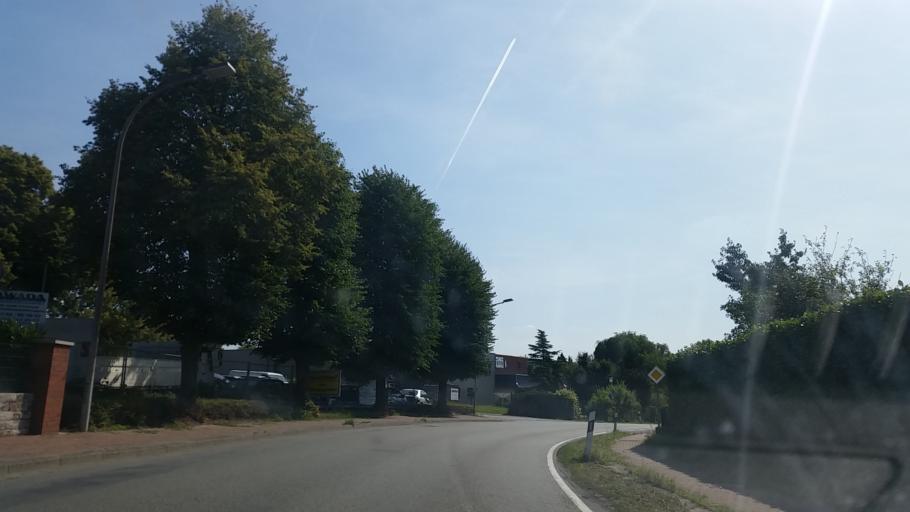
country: DE
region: Lower Saxony
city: Ankum
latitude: 52.5406
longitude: 7.8805
